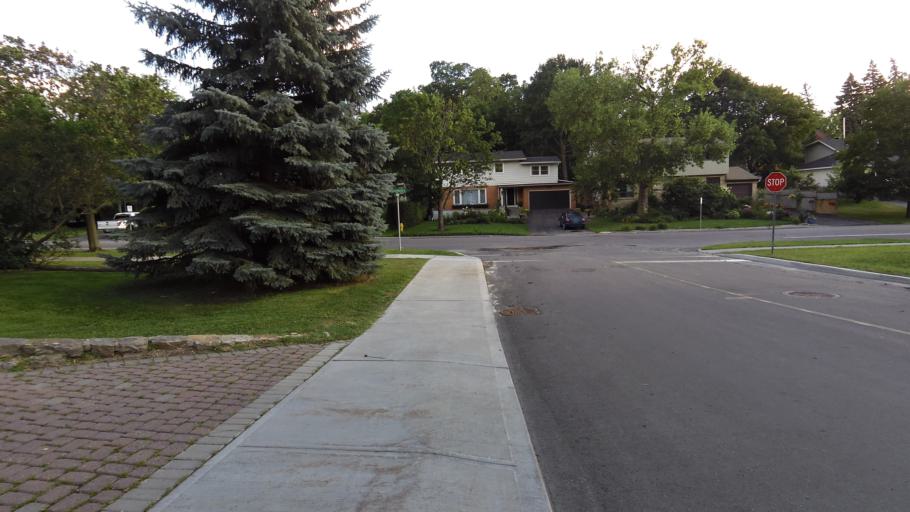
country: CA
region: Ontario
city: Ottawa
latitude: 45.3966
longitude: -75.7163
